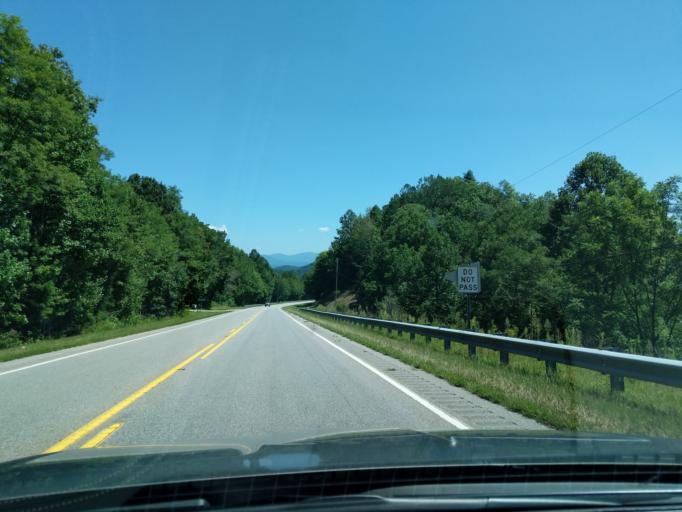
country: US
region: North Carolina
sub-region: Macon County
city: Franklin
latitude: 35.1371
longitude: -83.5043
